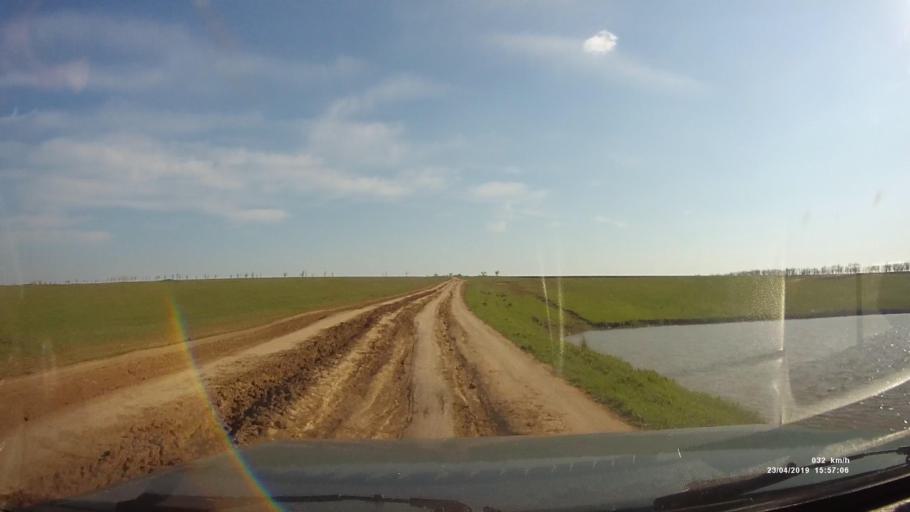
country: RU
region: Rostov
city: Remontnoye
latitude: 46.5337
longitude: 43.1104
